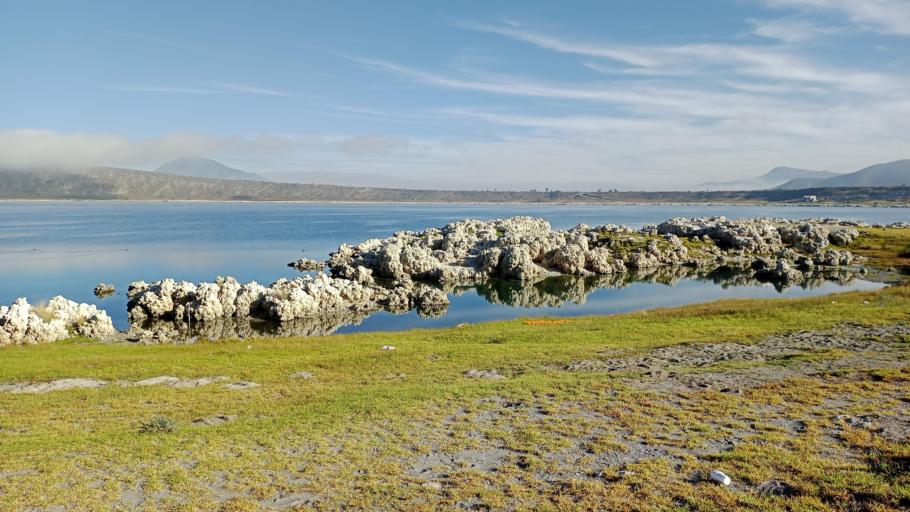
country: MX
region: Puebla
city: Guadalupe Victoria
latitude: 19.4065
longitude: -97.3999
